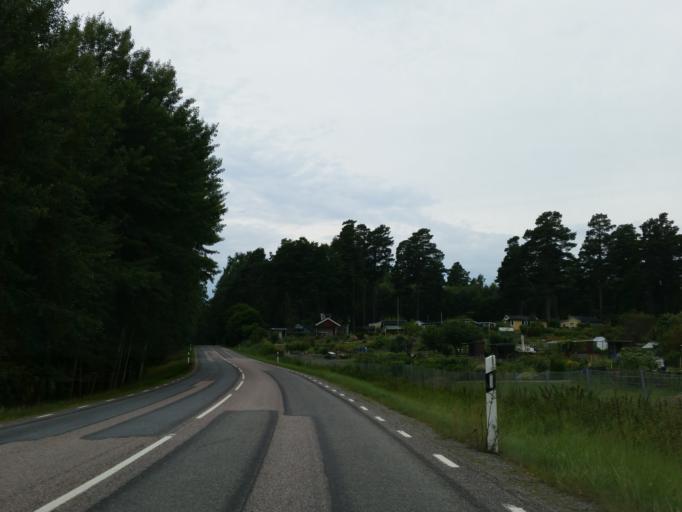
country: SE
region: Stockholm
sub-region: Sodertalje Kommun
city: Soedertaelje
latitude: 59.2025
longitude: 17.5642
